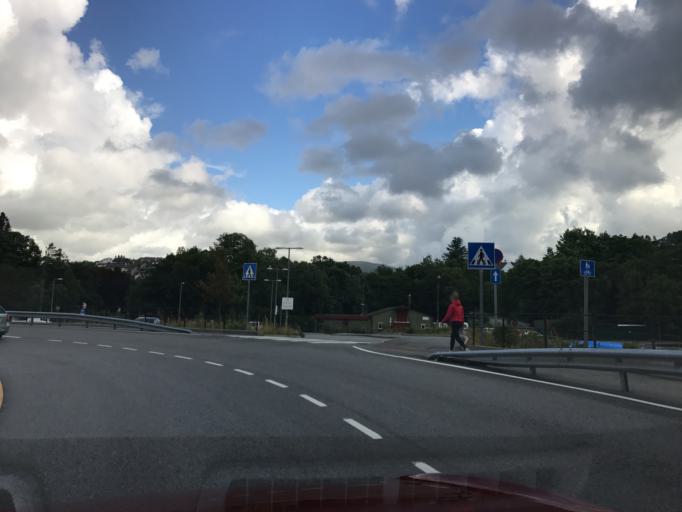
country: NO
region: Hordaland
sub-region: Bergen
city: Sandsli
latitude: 60.3129
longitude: 5.3585
